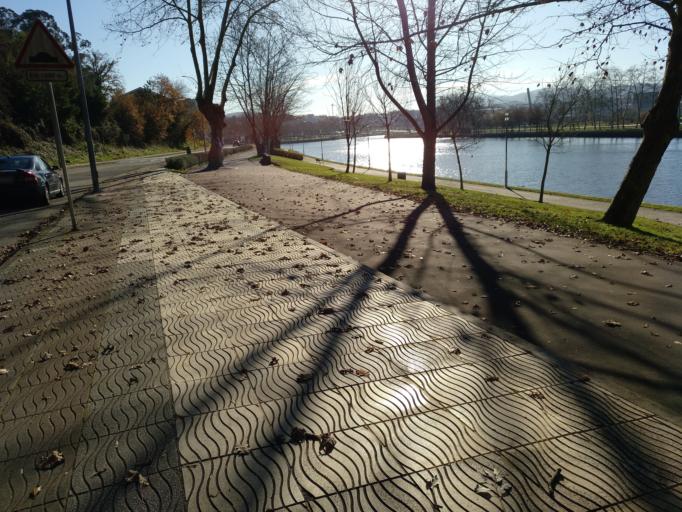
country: ES
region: Galicia
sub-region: Provincia de Pontevedra
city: Pontevedra
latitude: 42.4418
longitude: -8.6324
